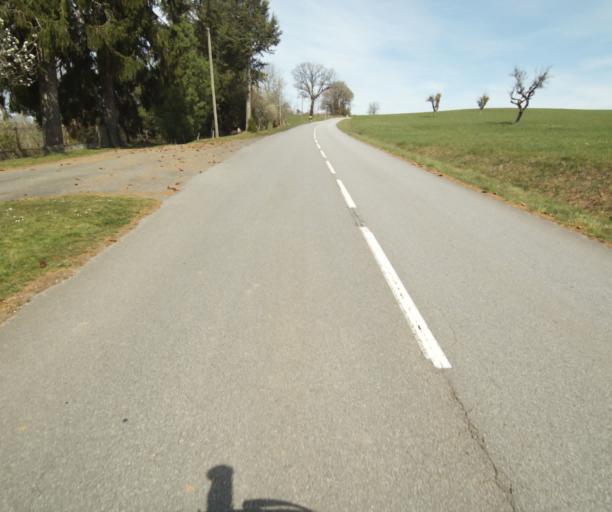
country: FR
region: Limousin
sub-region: Departement de la Correze
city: Correze
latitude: 45.3830
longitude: 1.8051
